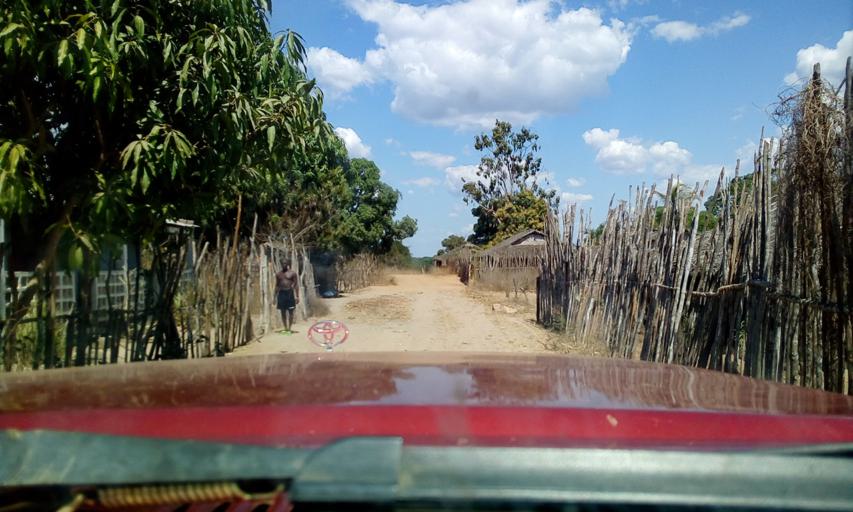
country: MG
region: Boeny
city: Sitampiky
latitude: -16.1251
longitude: 45.4706
